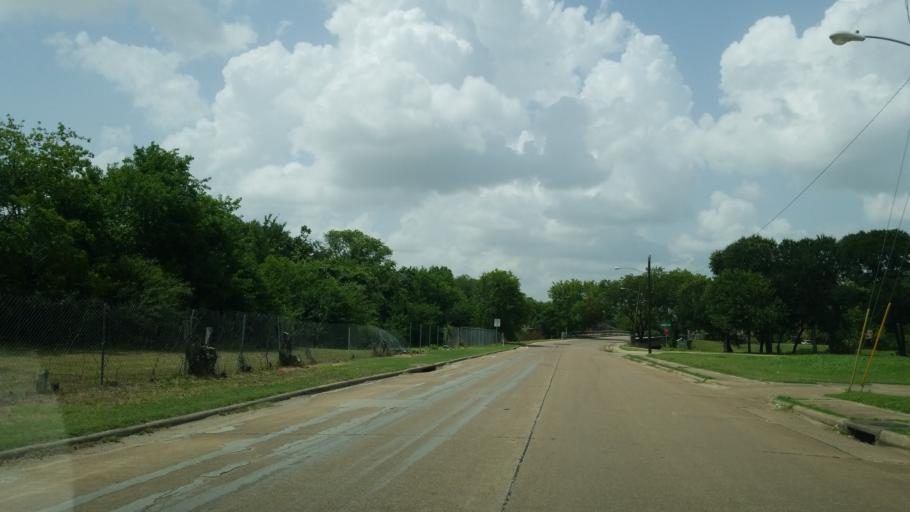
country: US
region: Texas
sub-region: Dallas County
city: Cockrell Hill
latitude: 32.7880
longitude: -96.8826
